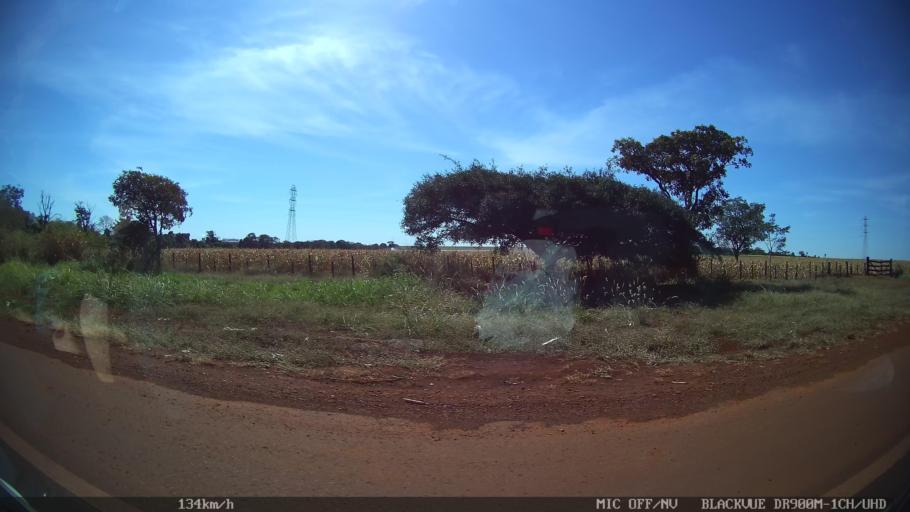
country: BR
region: Sao Paulo
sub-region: Guaira
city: Guaira
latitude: -20.4483
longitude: -48.1965
